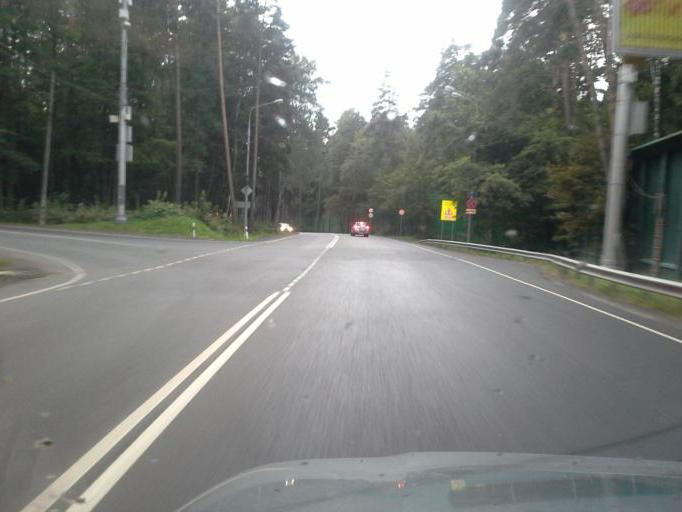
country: RU
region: Moskovskaya
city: Nikolina Gora
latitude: 55.7082
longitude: 37.0586
